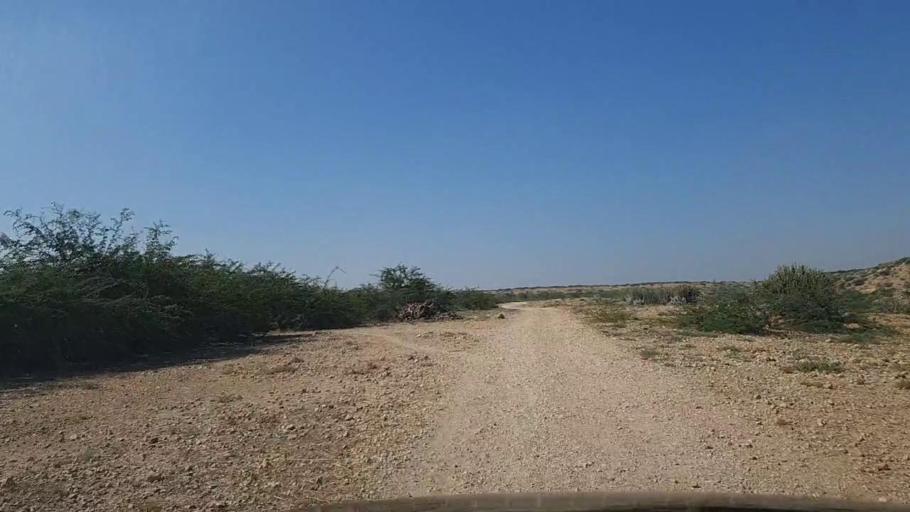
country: PK
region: Sindh
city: Thatta
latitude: 24.6288
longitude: 67.8640
